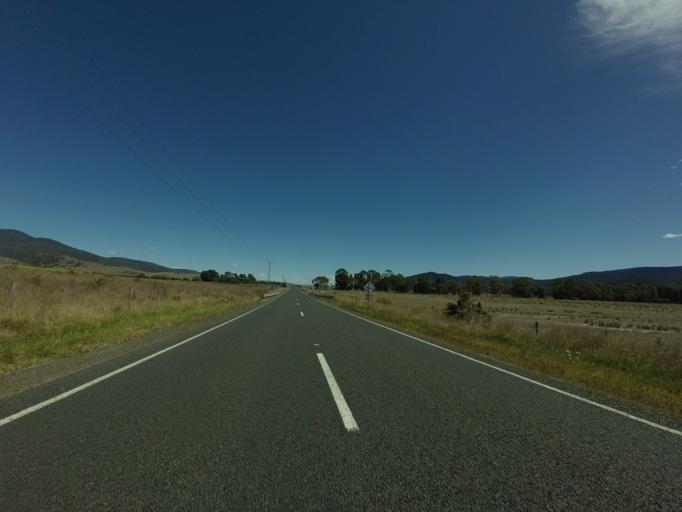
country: AU
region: Tasmania
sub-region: Break O'Day
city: St Helens
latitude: -41.7078
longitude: 147.8465
